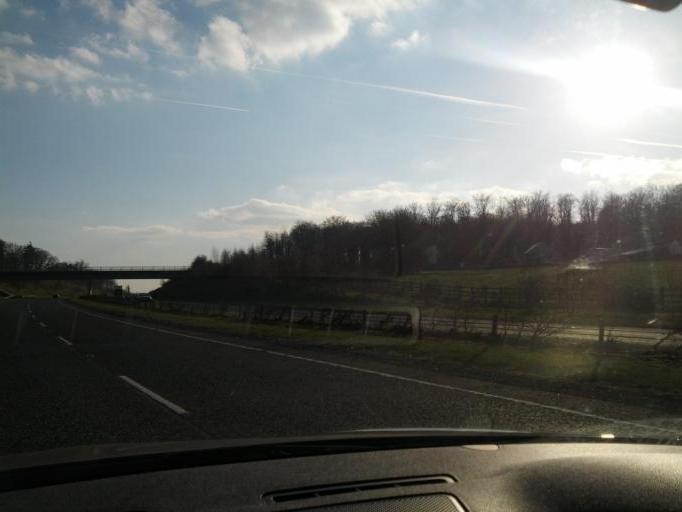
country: IE
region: Leinster
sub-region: Kildare
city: Monasterevin
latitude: 53.1237
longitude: -7.0394
